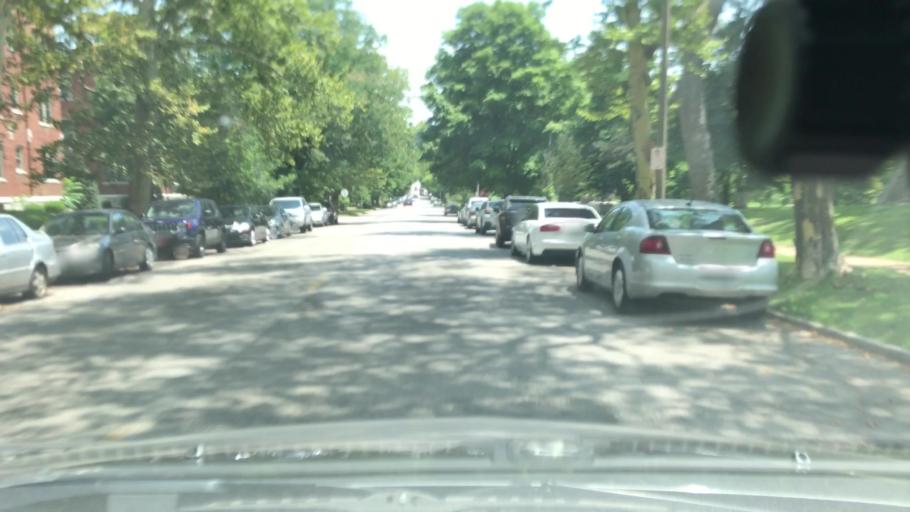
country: US
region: Missouri
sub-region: City of Saint Louis
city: St. Louis
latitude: 38.6083
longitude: -90.2528
